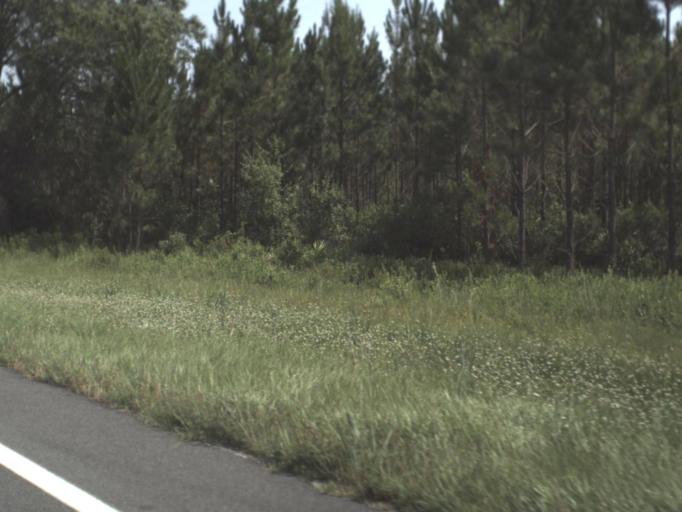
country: US
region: Florida
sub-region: Hamilton County
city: Jasper
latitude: 30.5807
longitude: -82.9988
